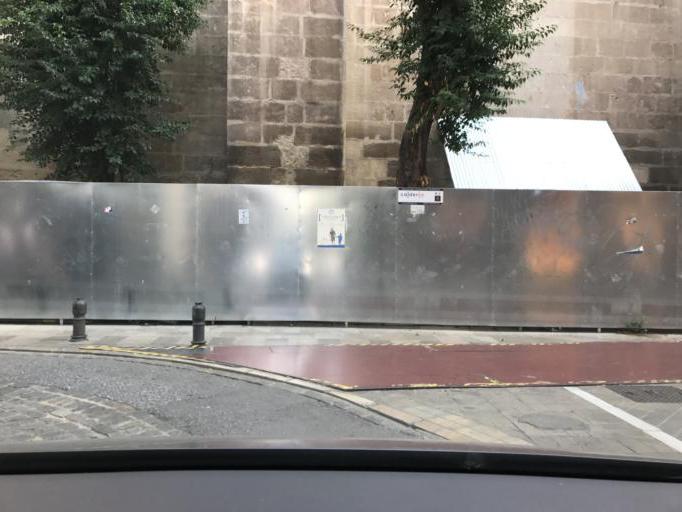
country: ES
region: Andalusia
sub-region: Provincia de Granada
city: Granada
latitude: 37.1769
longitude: -3.5997
